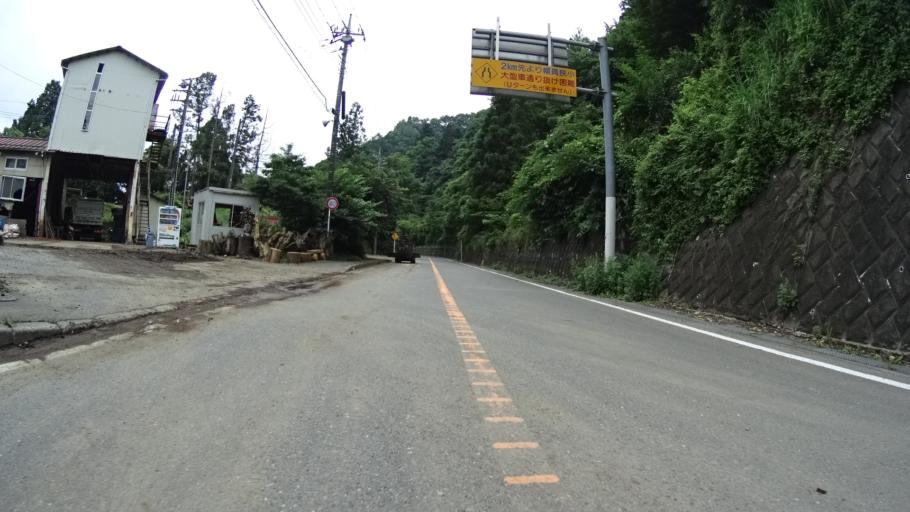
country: JP
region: Kanagawa
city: Hadano
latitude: 35.5185
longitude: 139.2311
